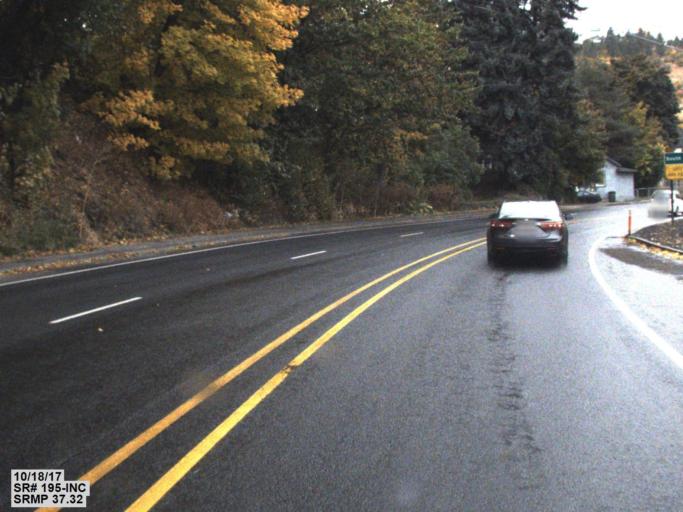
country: US
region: Washington
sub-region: Whitman County
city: Colfax
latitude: 46.8733
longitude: -117.3628
